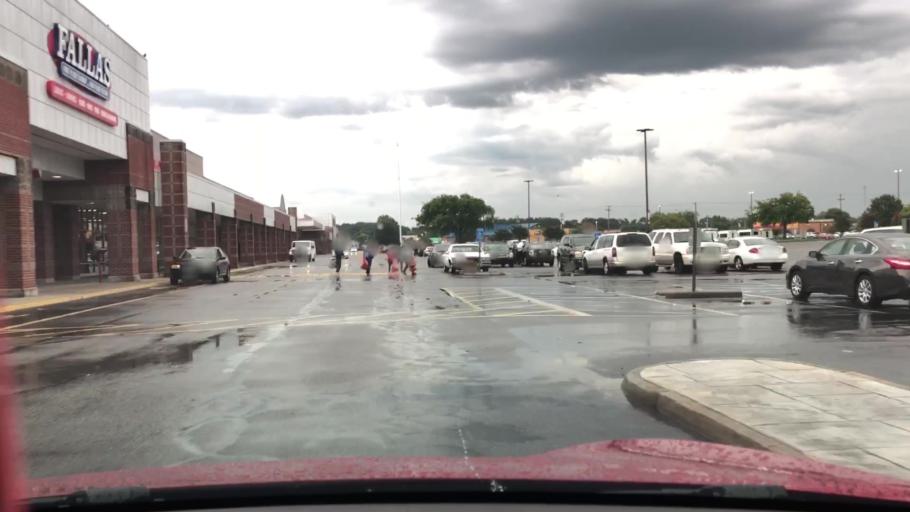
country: US
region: Virginia
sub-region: City of Chesapeake
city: Chesapeake
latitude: 36.8586
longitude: -76.2044
